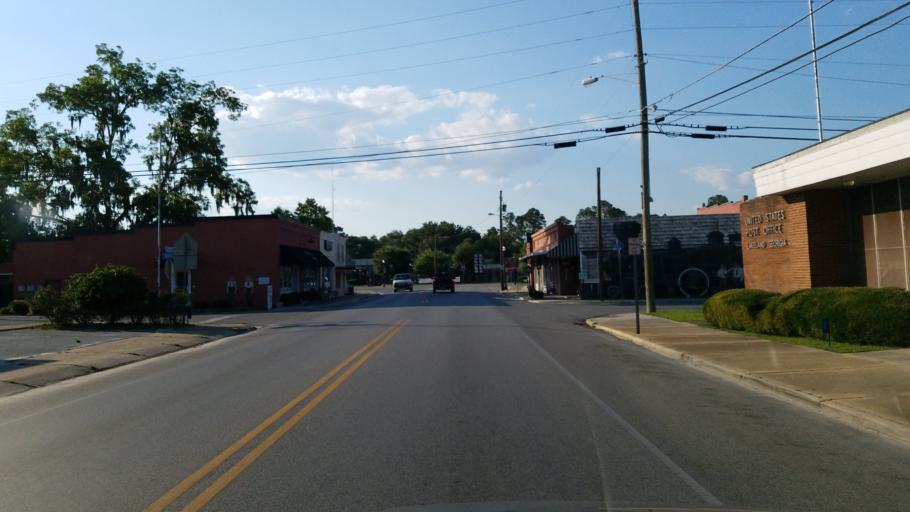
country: US
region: Georgia
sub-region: Lanier County
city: Lakeland
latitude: 31.0401
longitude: -83.0749
